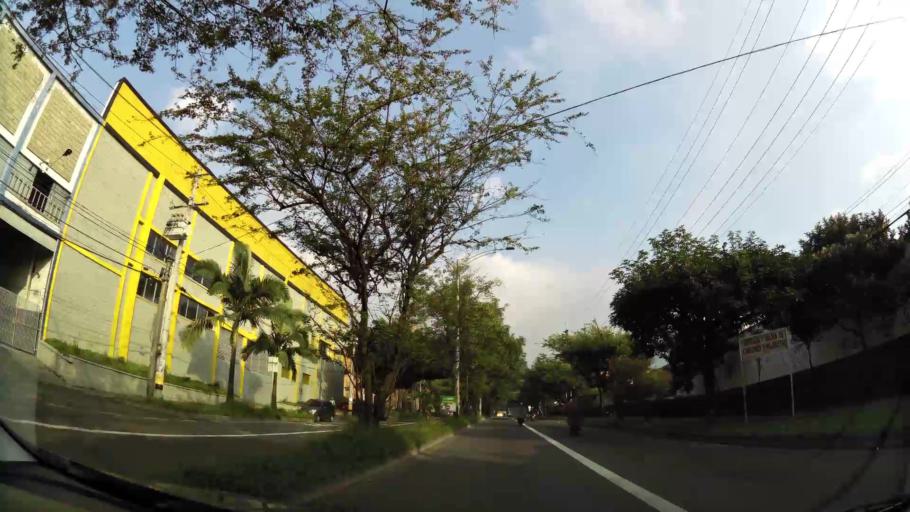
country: CO
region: Antioquia
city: Sabaneta
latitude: 6.1644
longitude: -75.6160
